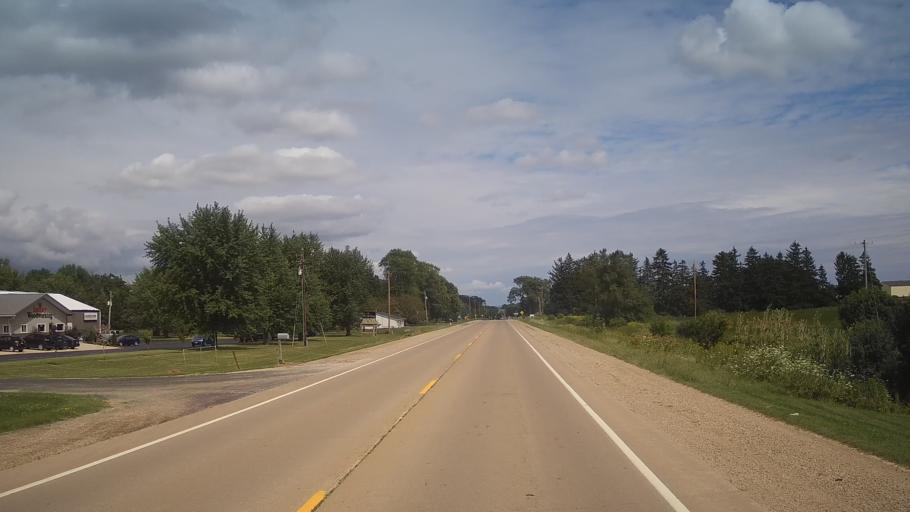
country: US
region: Wisconsin
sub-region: Winnebago County
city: Oshkosh
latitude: 44.0331
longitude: -88.6337
